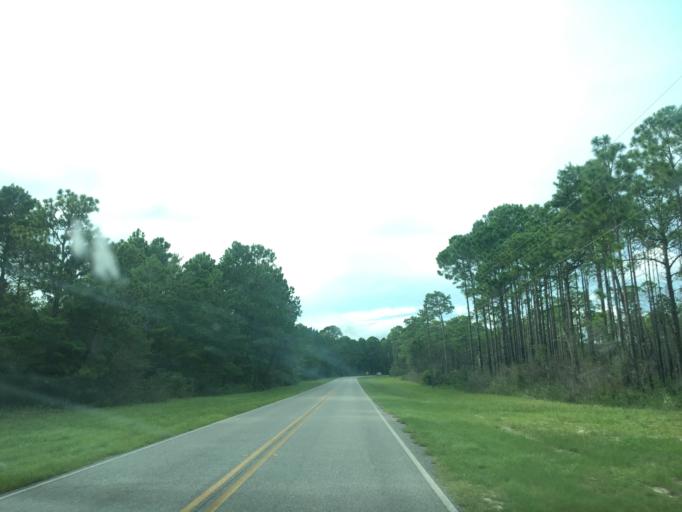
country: US
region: Florida
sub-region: Wakulla County
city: Crawfordville
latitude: 29.9267
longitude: -84.3767
